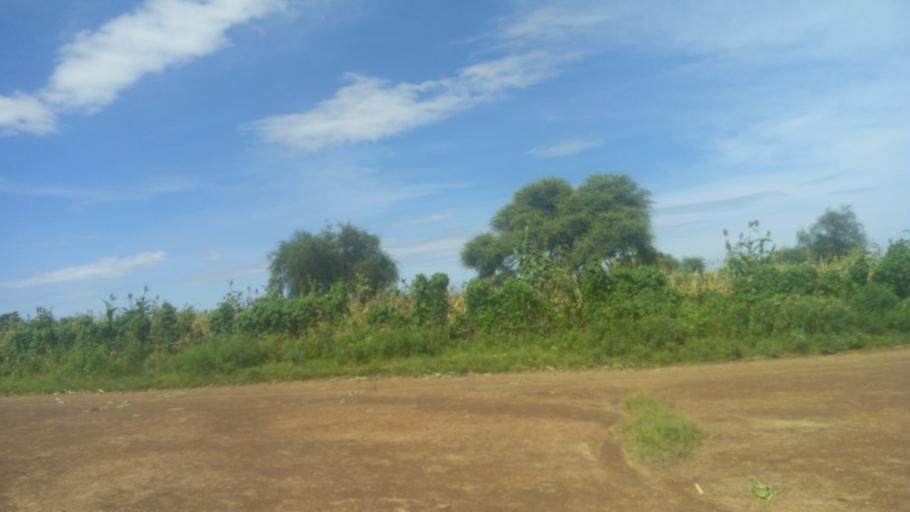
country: ML
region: Kayes
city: Yelimane
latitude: 14.8435
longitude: -10.7461
